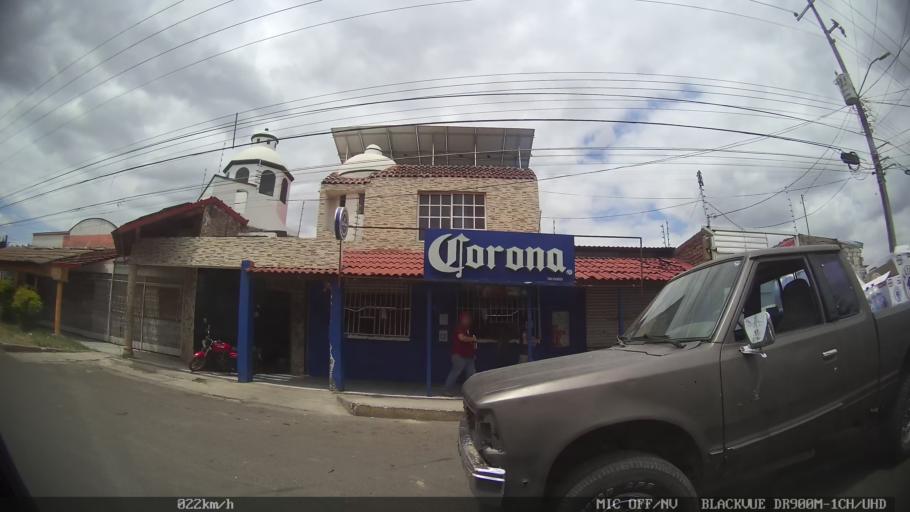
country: MX
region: Jalisco
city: Tonala
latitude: 20.6380
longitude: -103.2539
